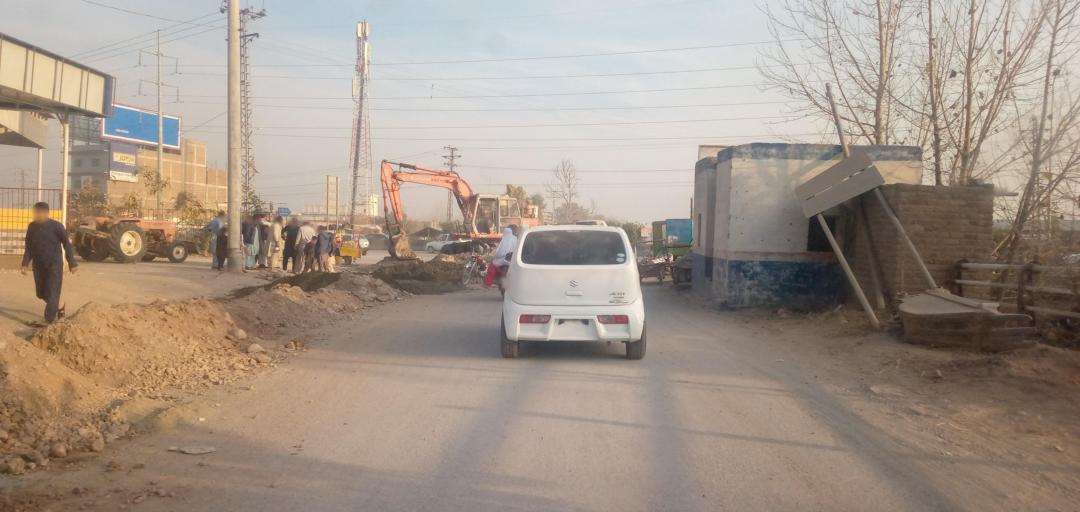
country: PK
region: Khyber Pakhtunkhwa
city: Peshawar
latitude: 33.9692
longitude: 71.5373
